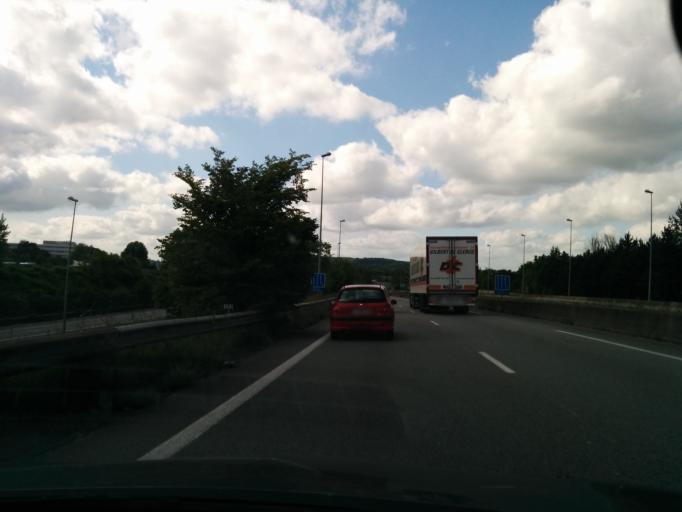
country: FR
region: Ile-de-France
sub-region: Departement des Yvelines
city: Villennes-sur-Seine
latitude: 48.9235
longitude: 2.0015
